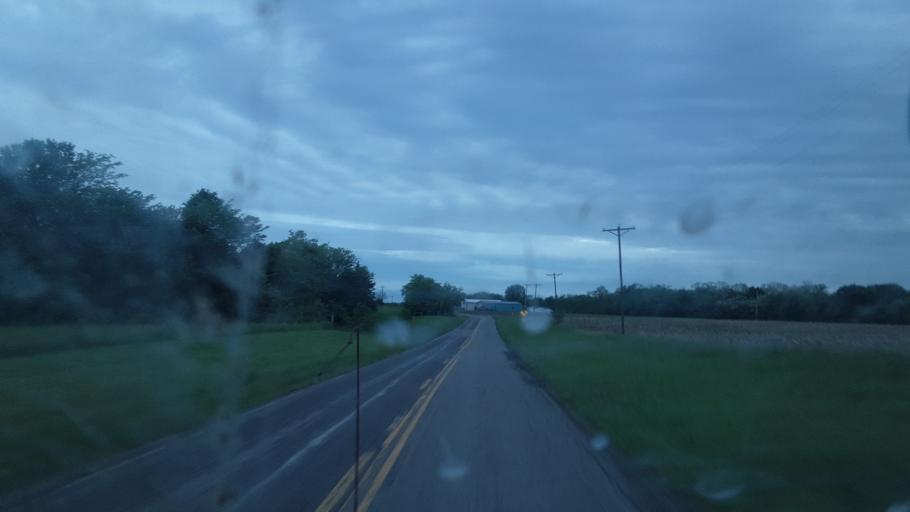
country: US
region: Missouri
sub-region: Clark County
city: Kahoka
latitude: 40.4389
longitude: -91.5996
